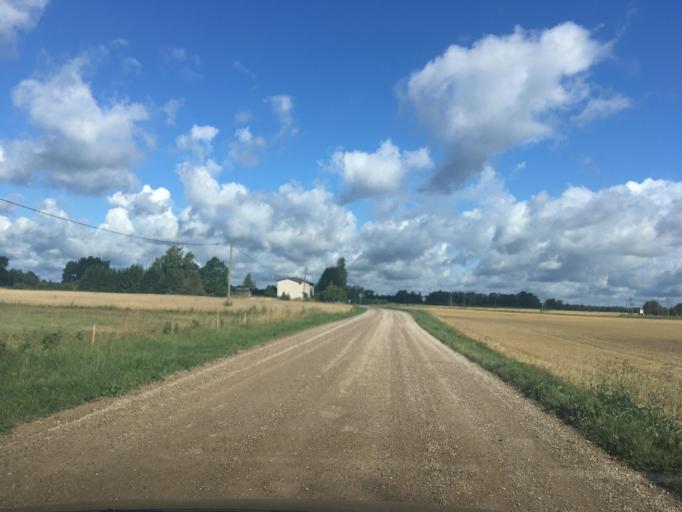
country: EE
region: Jogevamaa
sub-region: Poltsamaa linn
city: Poltsamaa
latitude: 58.4651
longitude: 25.9538
